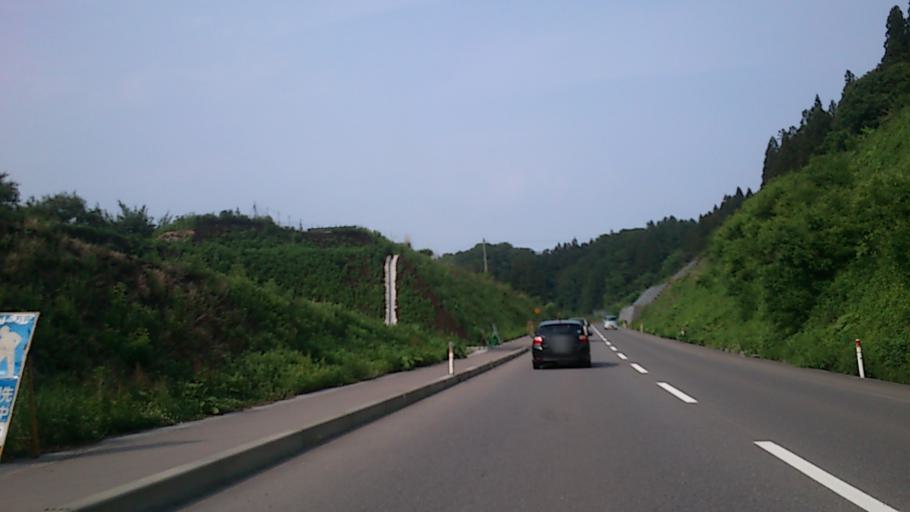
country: JP
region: Aomori
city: Hirosaki
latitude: 40.5706
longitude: 140.2965
